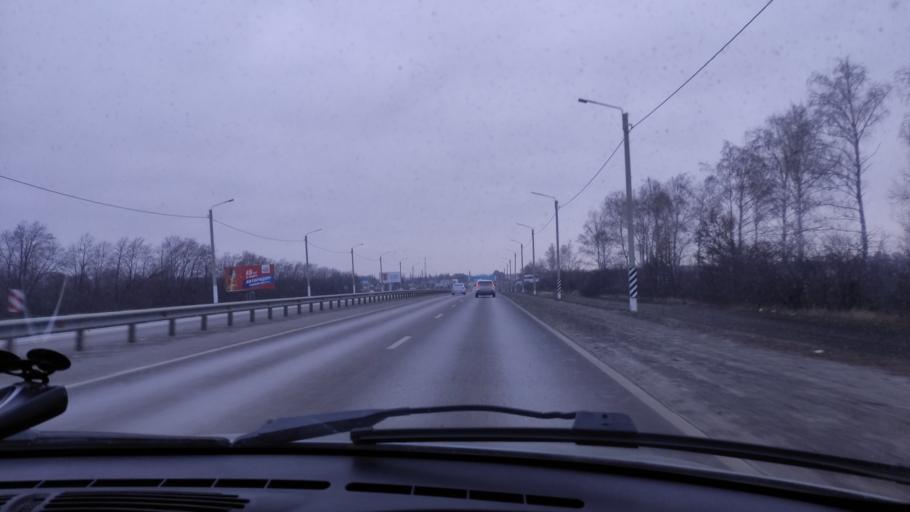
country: RU
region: Tambov
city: Komsomolets
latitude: 52.7271
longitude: 41.3369
